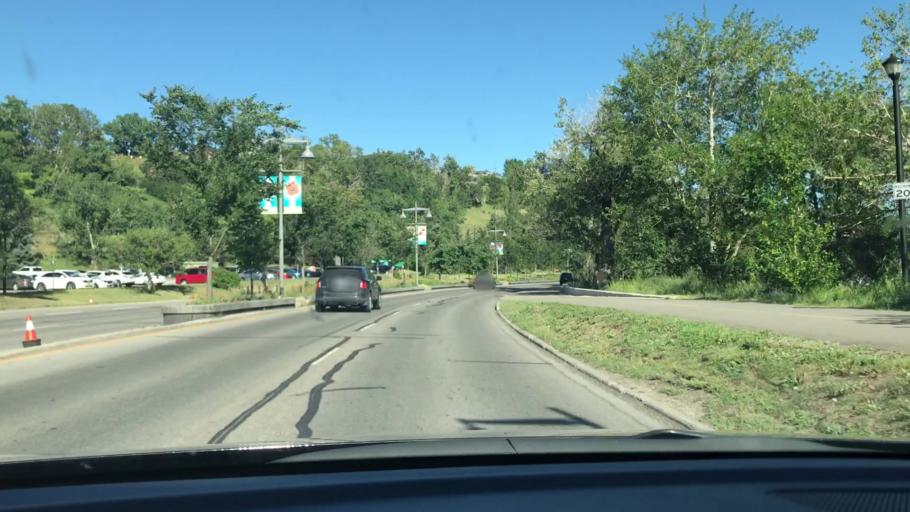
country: CA
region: Alberta
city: Calgary
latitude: 51.0574
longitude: -114.0683
